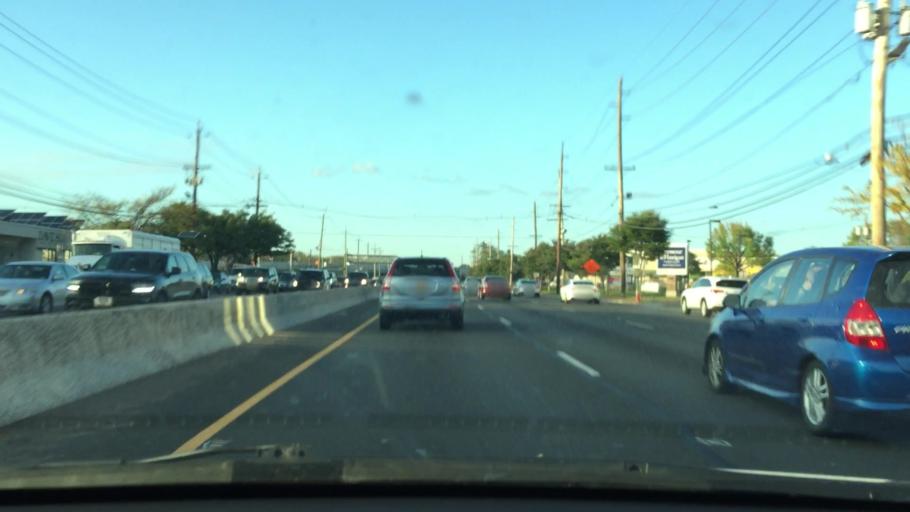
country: US
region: New Jersey
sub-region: Bergen County
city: Paramus
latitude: 40.9341
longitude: -74.0708
